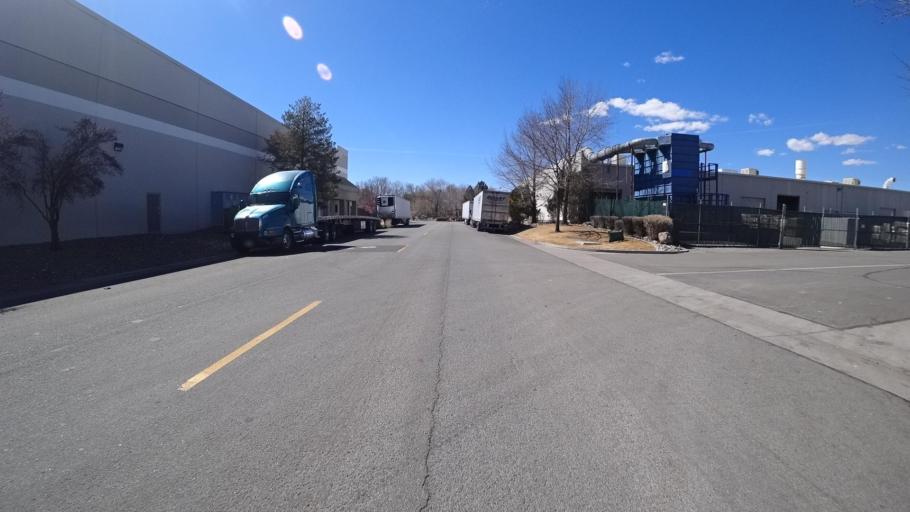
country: US
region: Nevada
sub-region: Washoe County
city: Sparks
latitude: 39.5392
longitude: -119.7134
